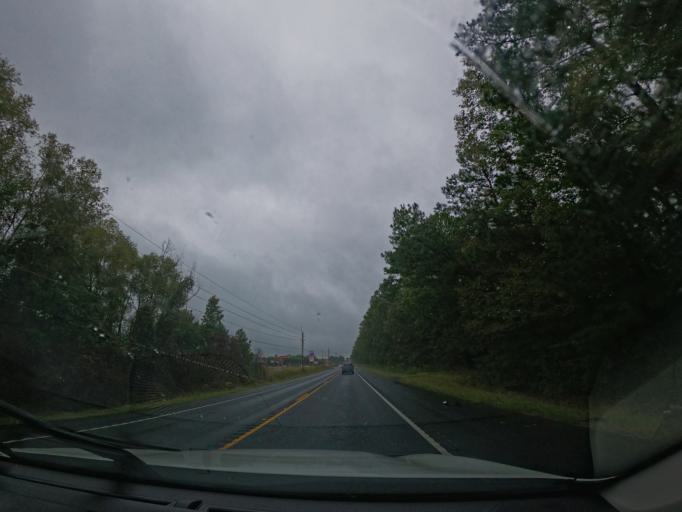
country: US
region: Louisiana
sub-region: Caddo Parish
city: Greenwood
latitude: 32.3959
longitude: -94.0063
